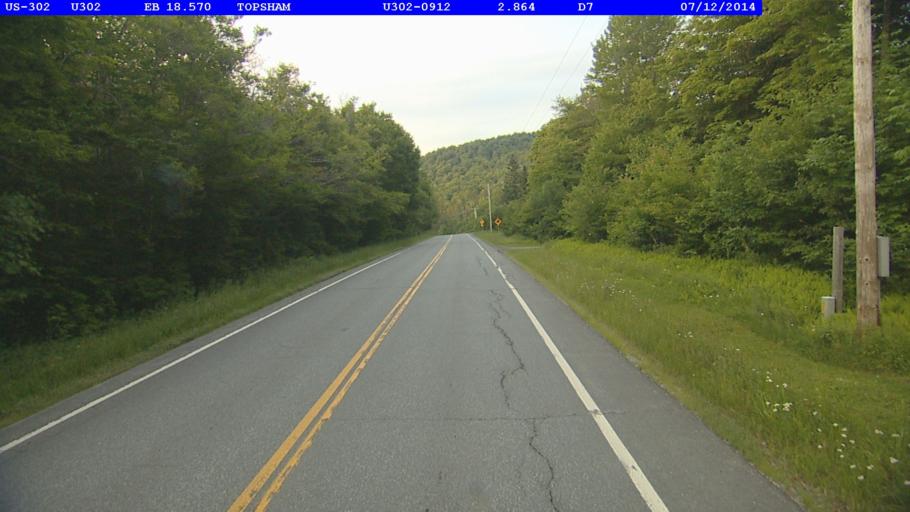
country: US
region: Vermont
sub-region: Washington County
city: Barre
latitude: 44.1764
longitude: -72.3005
